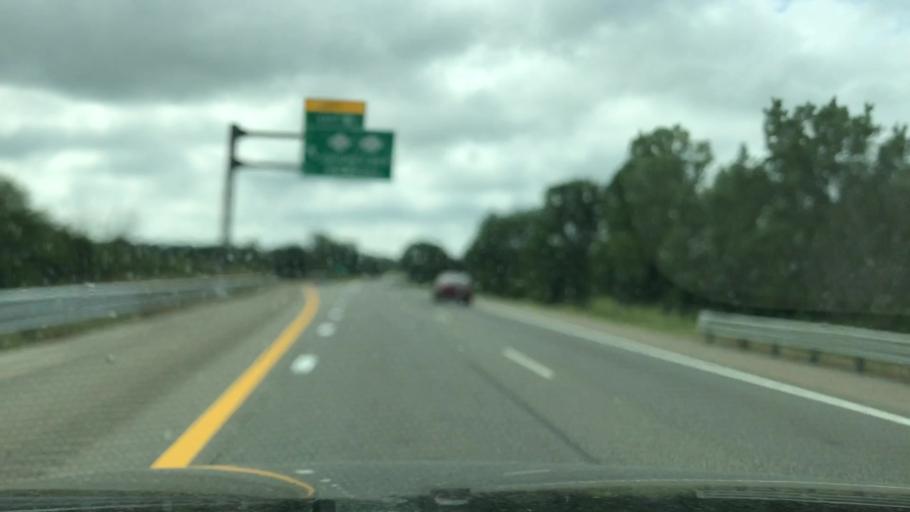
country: US
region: Michigan
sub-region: Muskegon County
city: Fruitport
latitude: 43.0735
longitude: -86.0760
